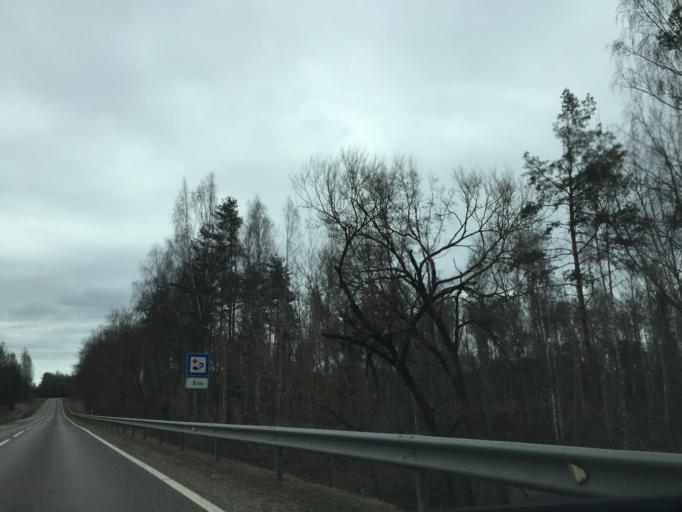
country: LV
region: Kraslavas Rajons
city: Kraslava
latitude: 55.9034
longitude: 27.1115
